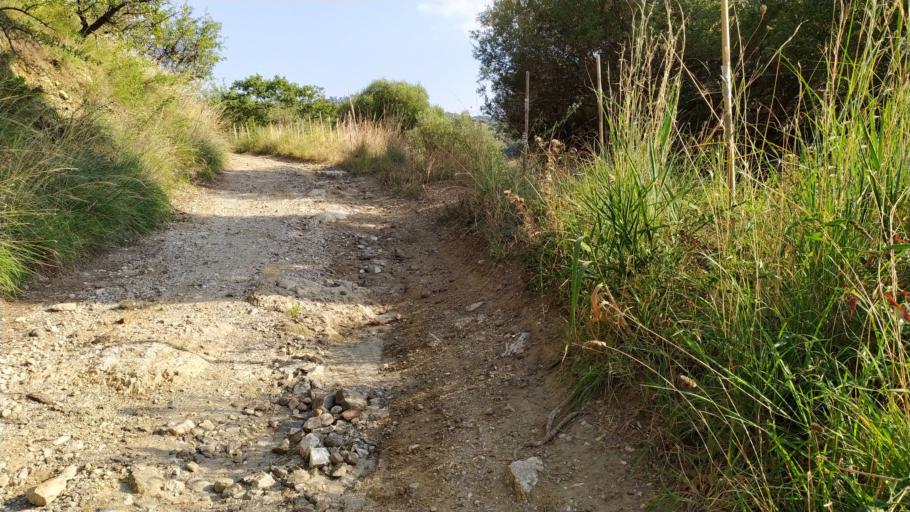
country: IT
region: Sicily
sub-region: Messina
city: San Pier Niceto
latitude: 38.1604
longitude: 15.3349
